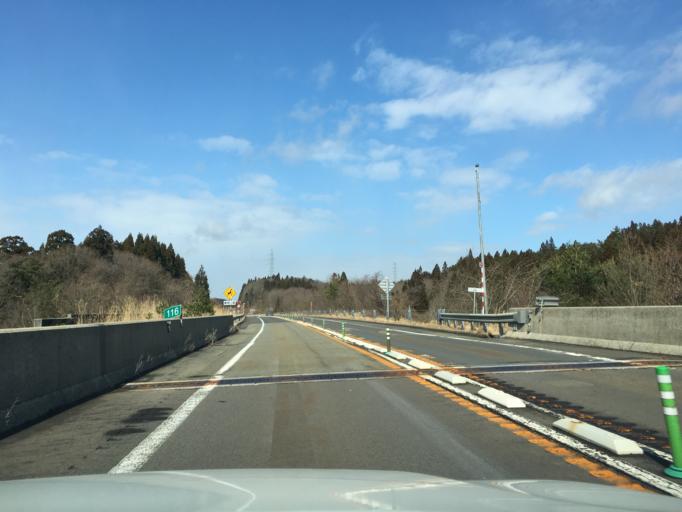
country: JP
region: Akita
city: Akita
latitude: 39.7400
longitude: 140.1698
